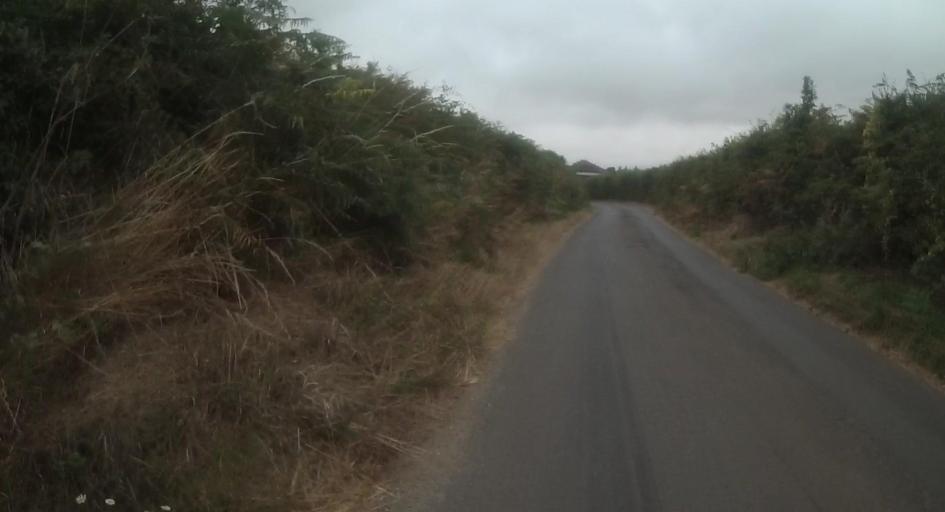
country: GB
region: England
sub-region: Dorset
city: Bovington Camp
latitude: 50.7340
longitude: -2.2085
